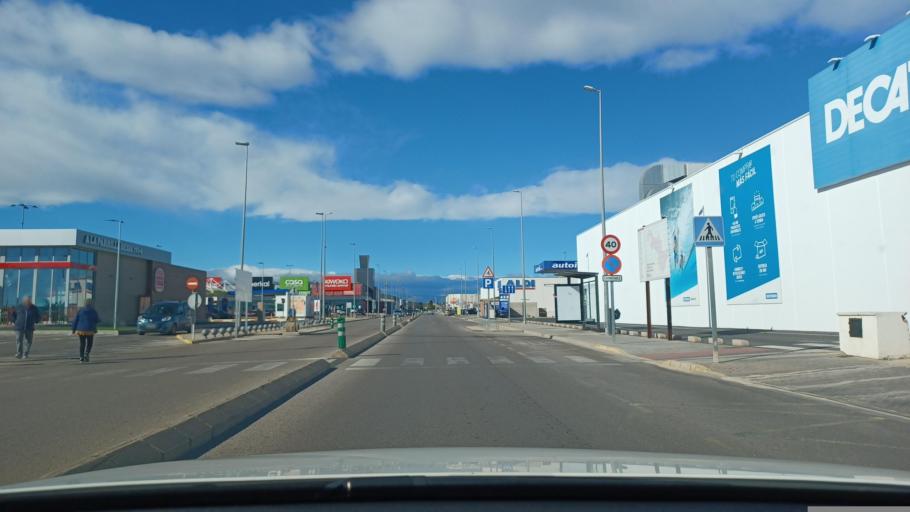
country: ES
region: Valencia
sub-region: Provincia de Castello
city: Vinaros
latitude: 40.4548
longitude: 0.4530
